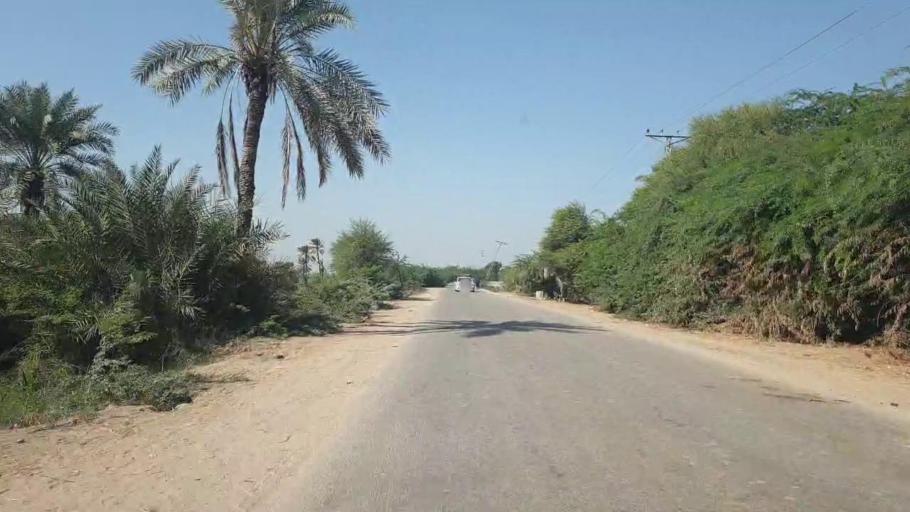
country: PK
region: Sindh
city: Talhar
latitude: 24.8922
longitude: 68.8232
